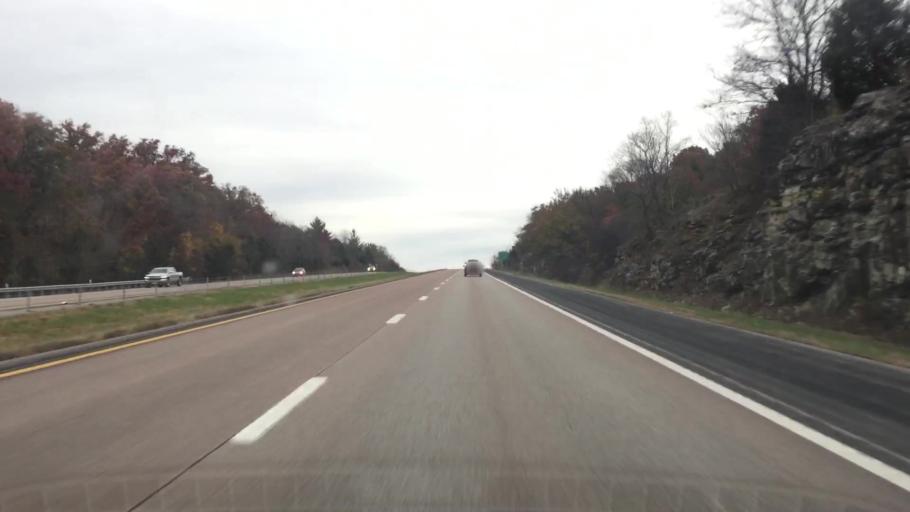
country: US
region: Missouri
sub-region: Boone County
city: Ashland
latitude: 38.6901
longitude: -92.2549
